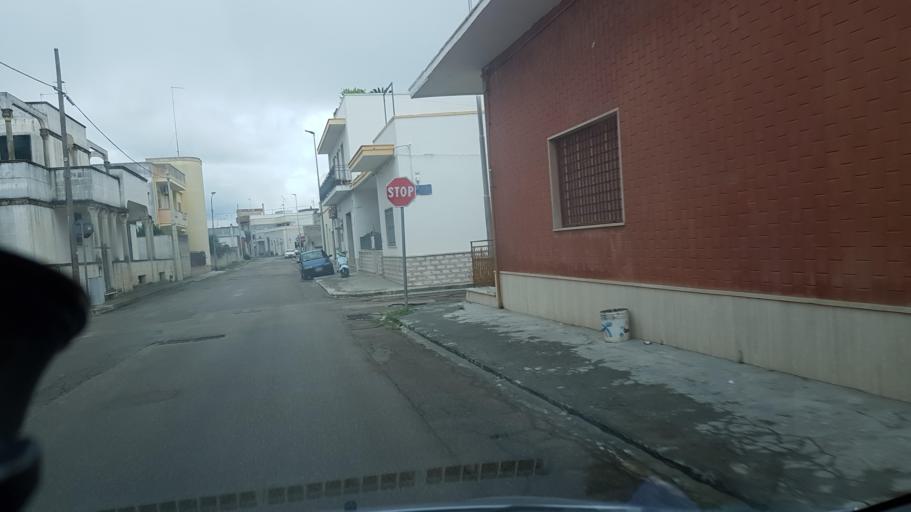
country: IT
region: Apulia
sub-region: Provincia di Lecce
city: Carmiano
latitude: 40.3504
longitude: 18.0418
